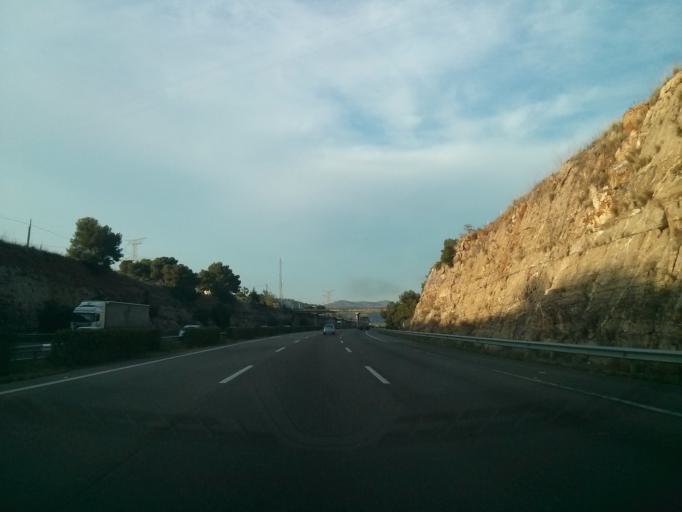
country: ES
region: Valencia
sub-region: Provincia de Valencia
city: Petres
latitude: 39.6619
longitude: -0.3050
